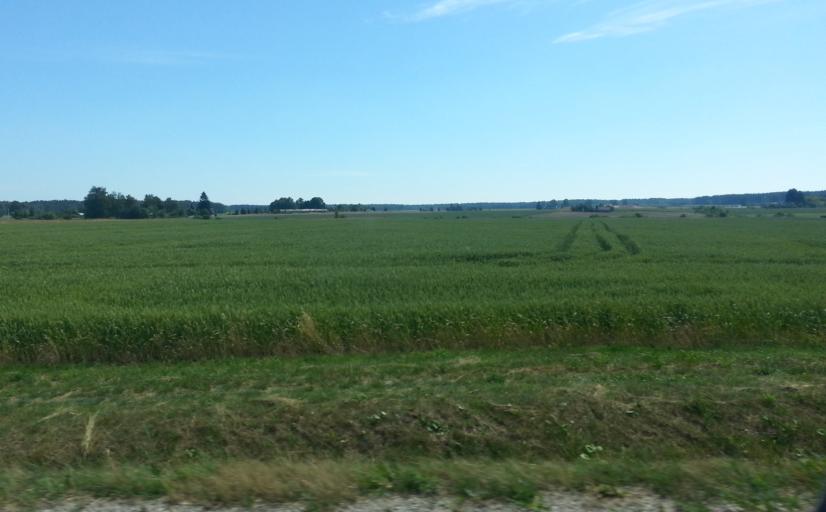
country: LT
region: Panevezys
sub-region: Panevezys City
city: Panevezys
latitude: 55.8516
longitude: 24.3510
